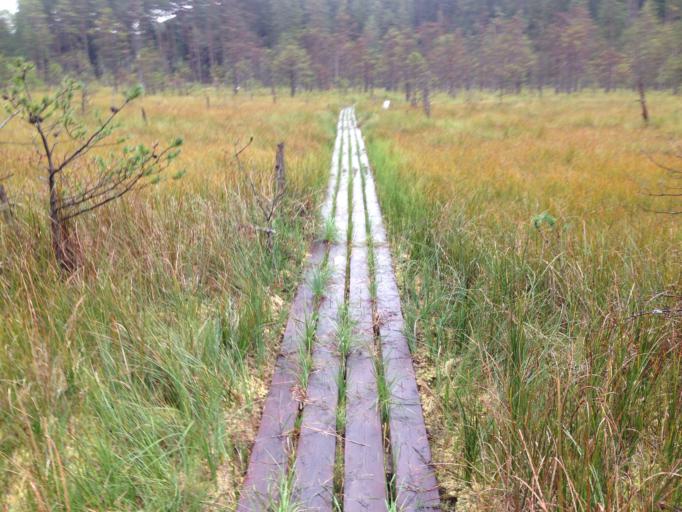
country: PL
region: Pomeranian Voivodeship
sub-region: Powiat bytowski
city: Czarna Dabrowka
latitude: 54.3801
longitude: 17.5419
